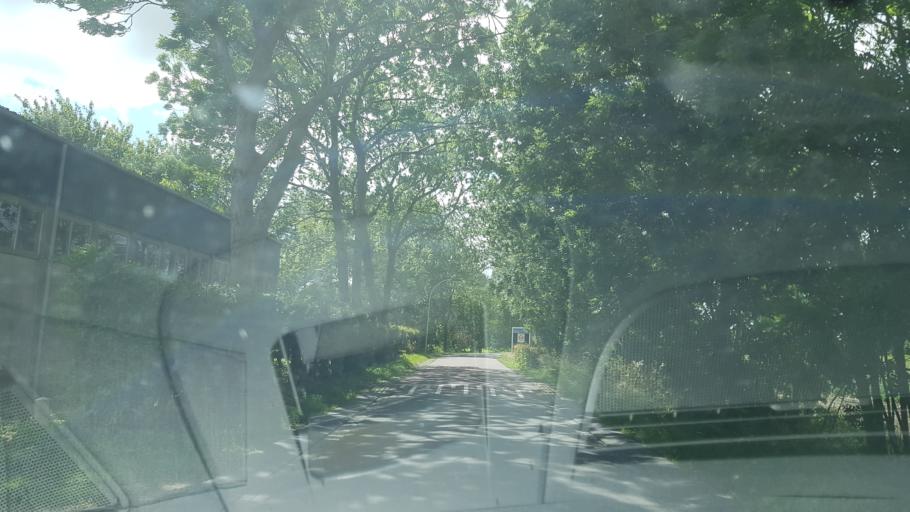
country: NL
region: Groningen
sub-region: Gemeente Winsum
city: Winsum
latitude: 53.3931
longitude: 6.5056
